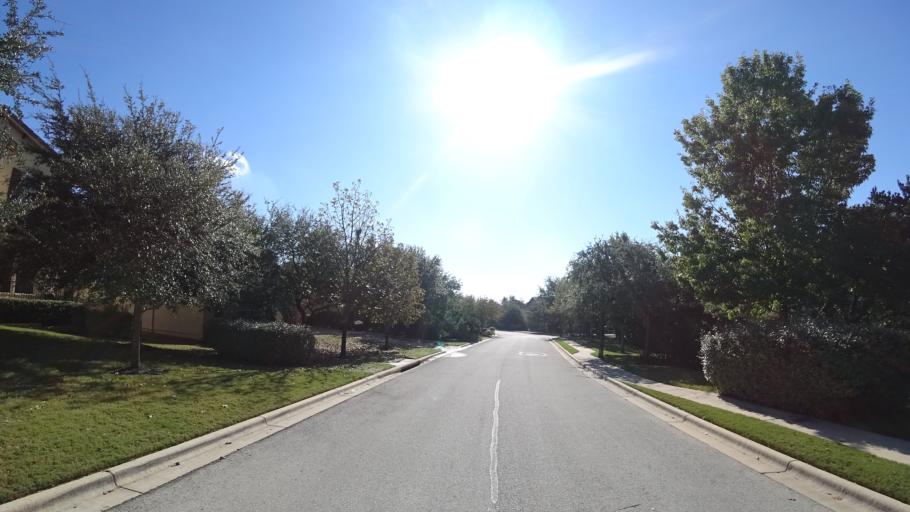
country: US
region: Texas
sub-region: Travis County
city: Barton Creek
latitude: 30.3544
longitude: -97.8864
